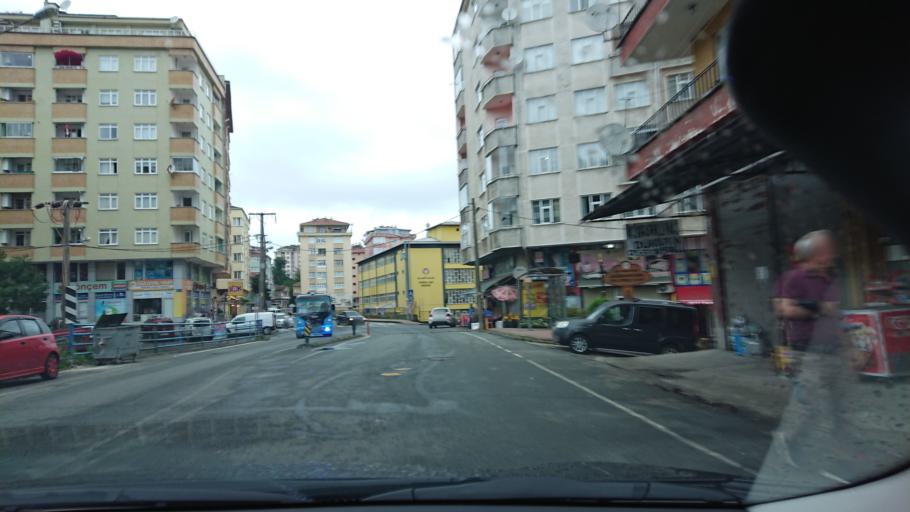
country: TR
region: Rize
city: Rize
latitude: 41.0308
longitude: 40.5106
